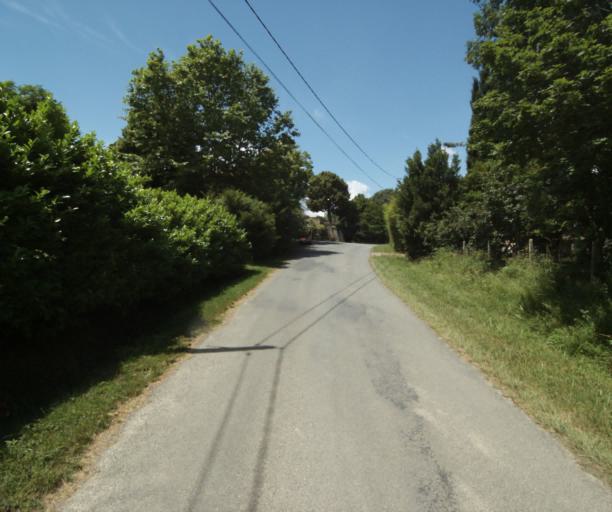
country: FR
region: Midi-Pyrenees
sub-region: Departement du Tarn
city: Puylaurens
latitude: 43.5250
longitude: 2.0265
